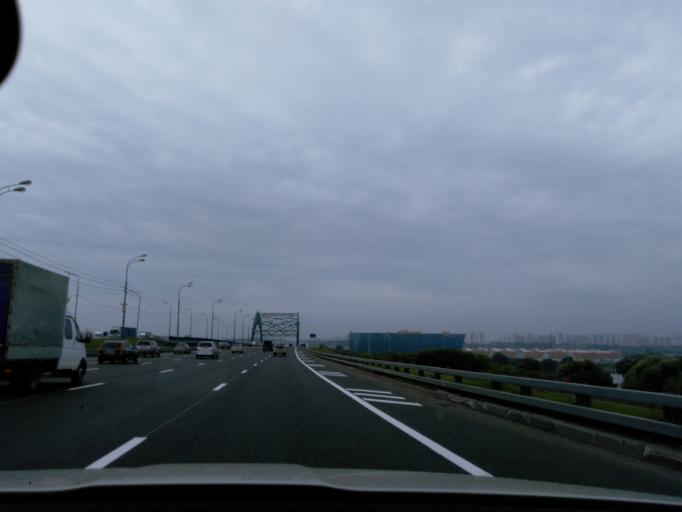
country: RU
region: Moskovskaya
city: Alekseyevka
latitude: 55.6259
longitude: 37.7964
